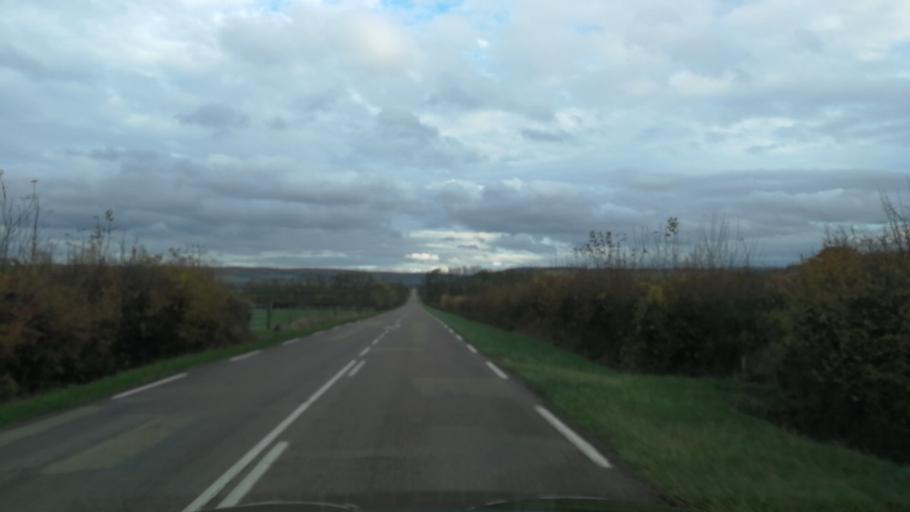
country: FR
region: Bourgogne
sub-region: Departement de la Cote-d'Or
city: Saulieu
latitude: 47.2696
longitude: 4.3608
